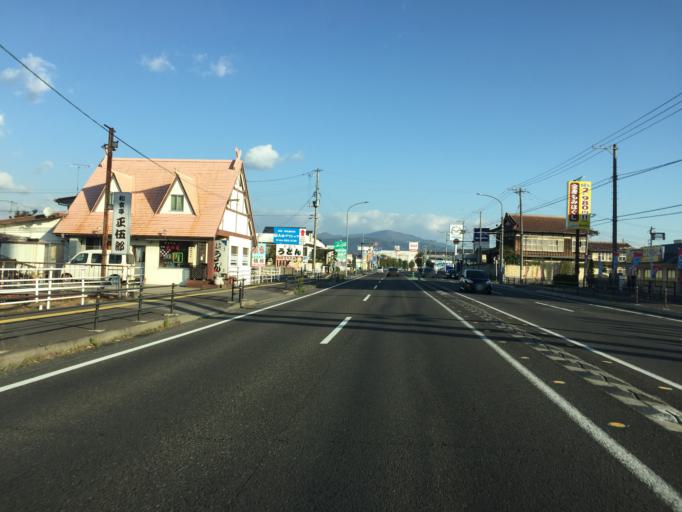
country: JP
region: Fukushima
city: Fukushima-shi
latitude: 37.7849
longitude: 140.4872
